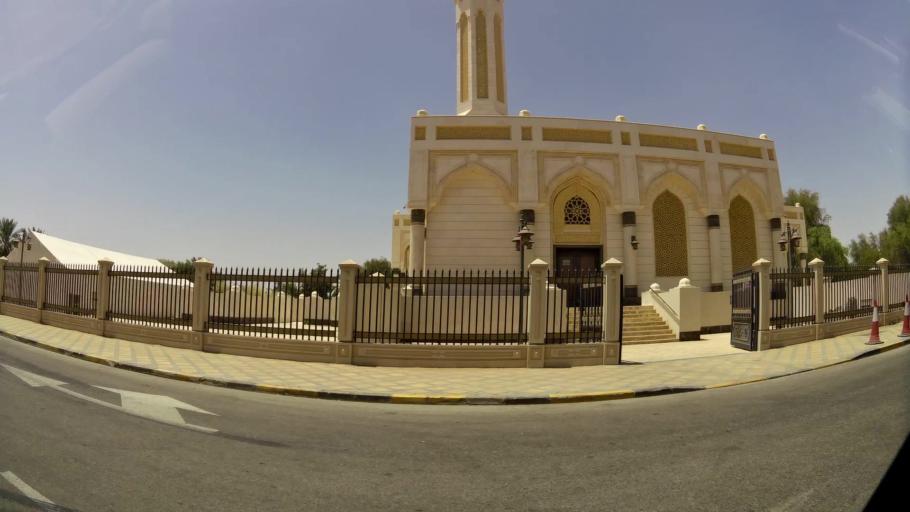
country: OM
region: Al Buraimi
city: Al Buraymi
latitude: 24.2740
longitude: 55.7413
